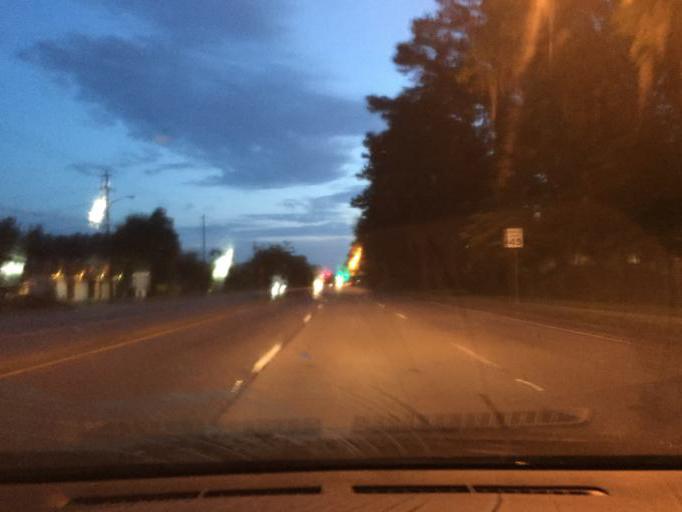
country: US
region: Georgia
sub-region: Chatham County
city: Isle of Hope
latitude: 32.0174
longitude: -81.1120
